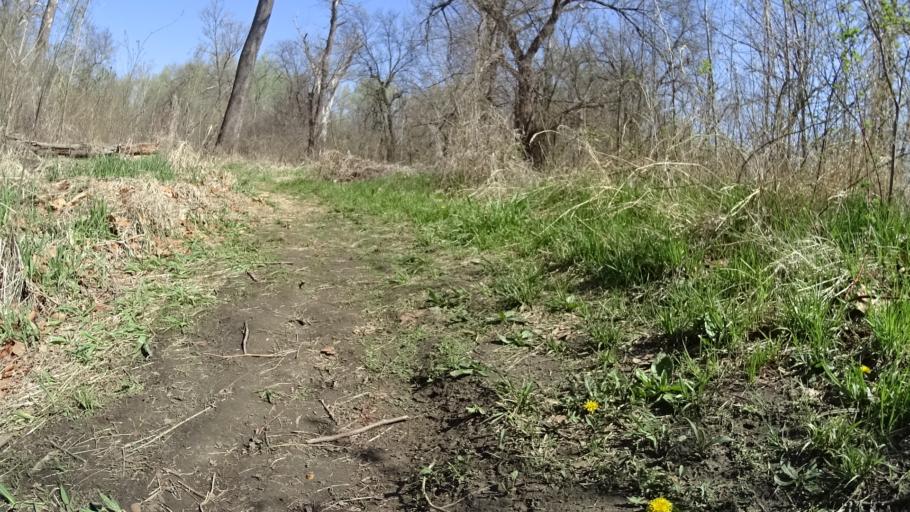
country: US
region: Nebraska
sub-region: Sarpy County
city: Bellevue
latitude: 41.1796
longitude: -95.8934
